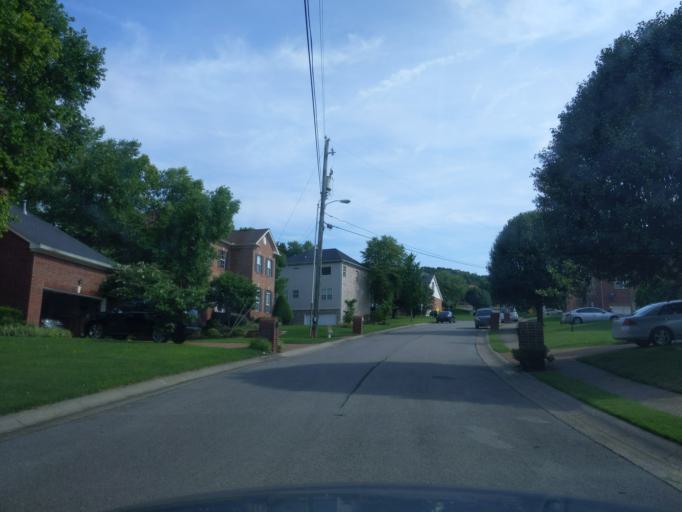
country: US
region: Tennessee
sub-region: Williamson County
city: Brentwood Estates
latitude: 36.0186
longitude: -86.7397
